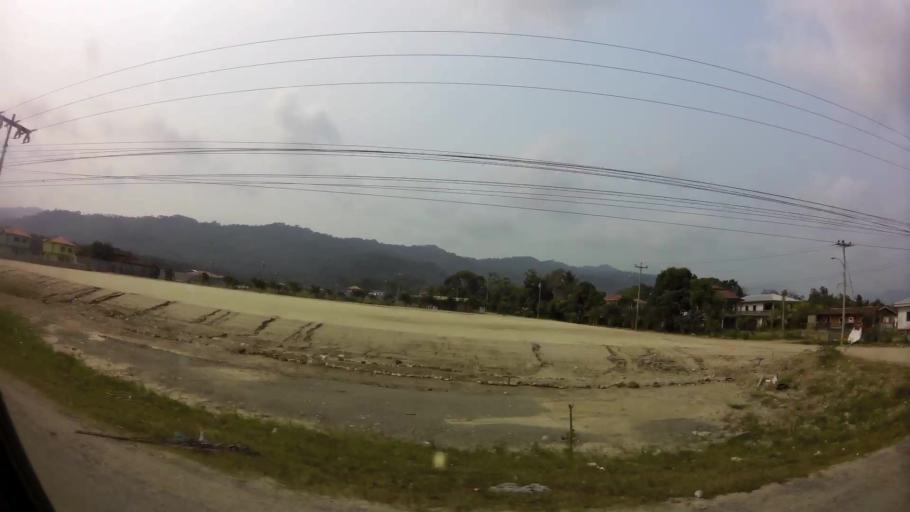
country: HN
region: Atlantida
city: Tela
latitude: 15.7637
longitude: -87.4751
